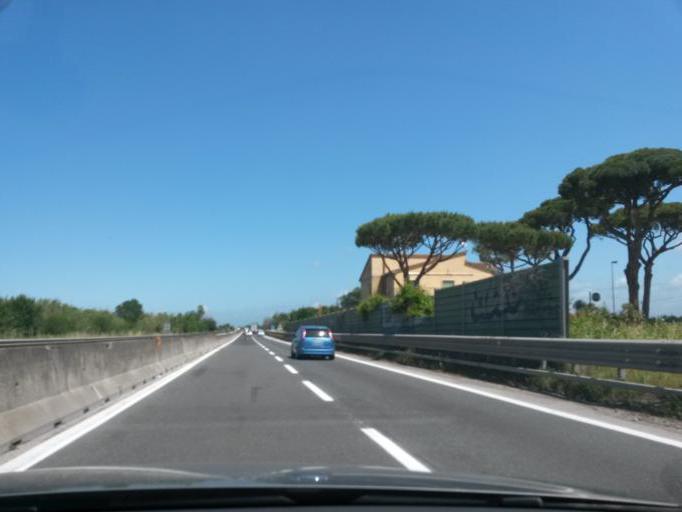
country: IT
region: Tuscany
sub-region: Provincia di Livorno
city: Donoratico
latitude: 43.2168
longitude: 10.5616
